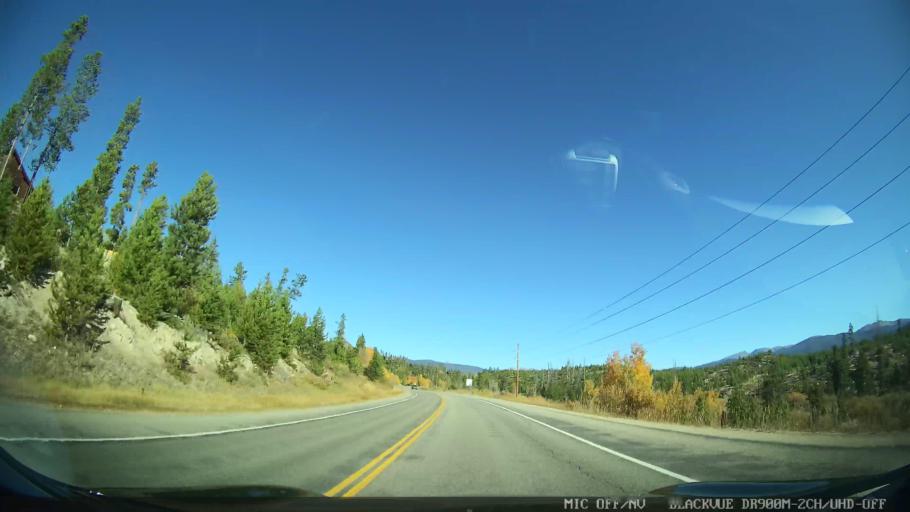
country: US
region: Colorado
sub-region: Grand County
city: Granby
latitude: 40.2083
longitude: -105.8602
